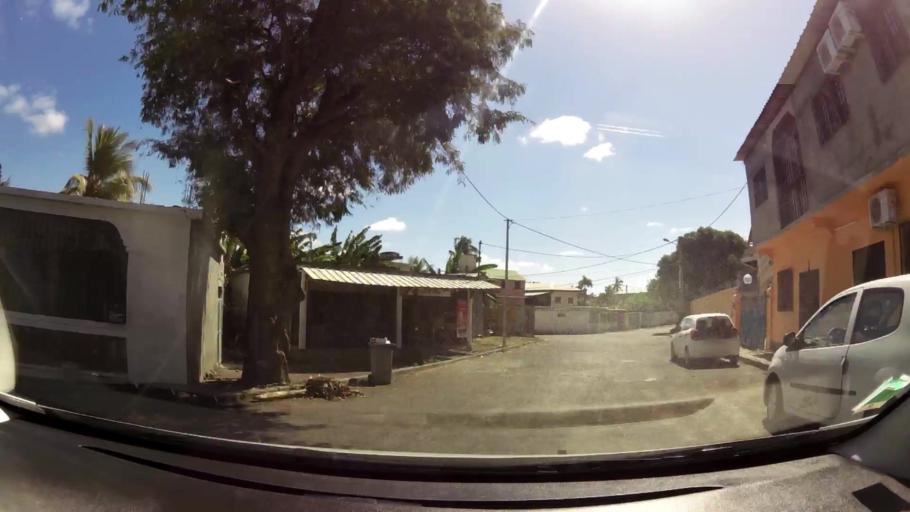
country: YT
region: Pamandzi
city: Pamandzi
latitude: -12.7913
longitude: 45.2812
